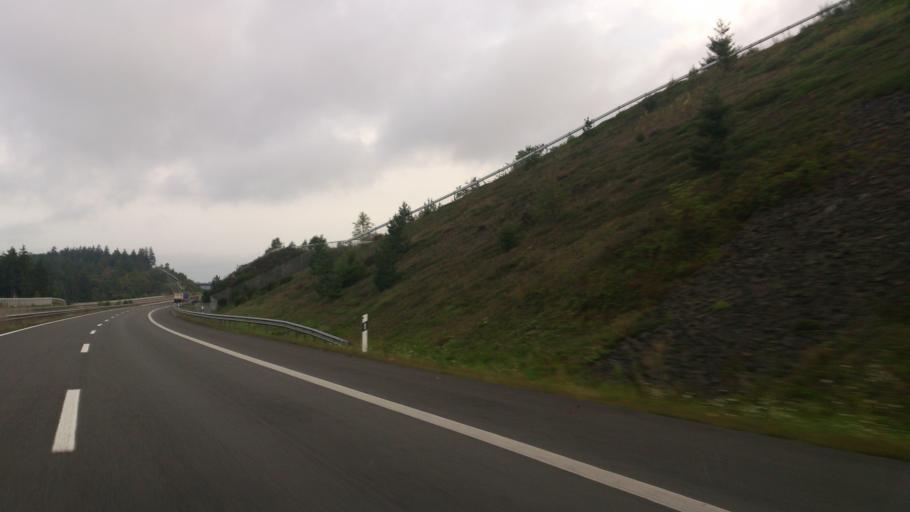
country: DE
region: Rheinland-Pfalz
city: Horscheid
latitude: 50.2140
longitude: 6.8674
